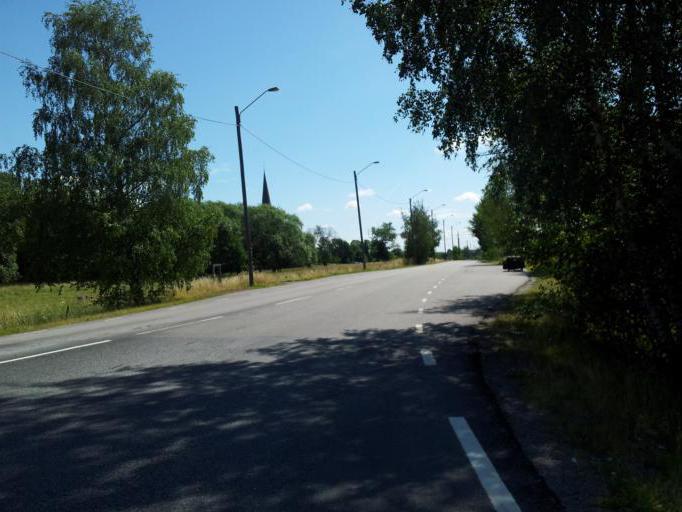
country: SE
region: Uppsala
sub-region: Uppsala Kommun
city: Uppsala
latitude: 59.8772
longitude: 17.6802
